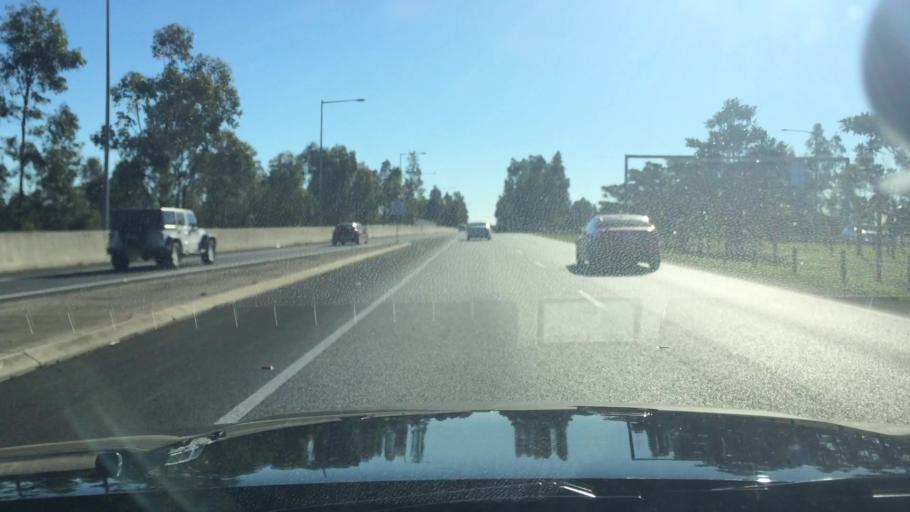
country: AU
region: New South Wales
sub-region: Blacktown
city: Doonside
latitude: -33.7914
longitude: 150.8558
